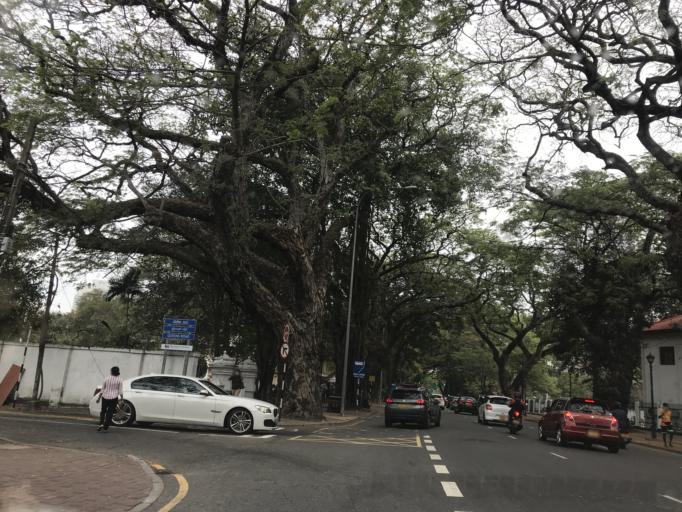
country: LK
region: Western
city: Colombo
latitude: 6.8997
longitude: 79.8597
